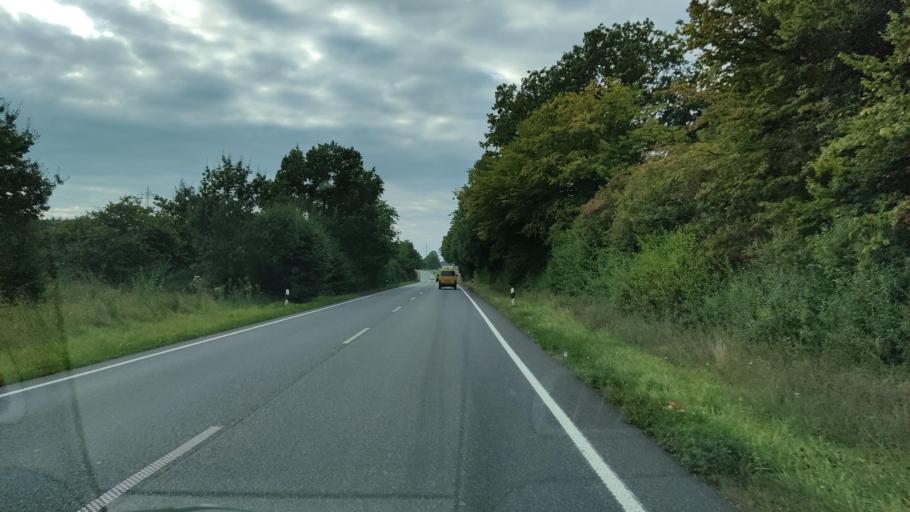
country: DE
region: Hesse
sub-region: Regierungsbezirk Giessen
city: Grossen Buseck
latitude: 50.5910
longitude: 8.7916
